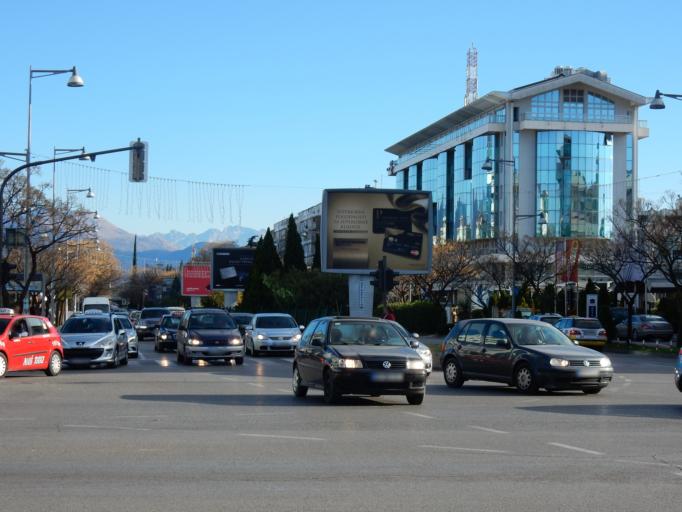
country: ME
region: Podgorica
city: Podgorica
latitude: 42.4436
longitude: 19.2456
